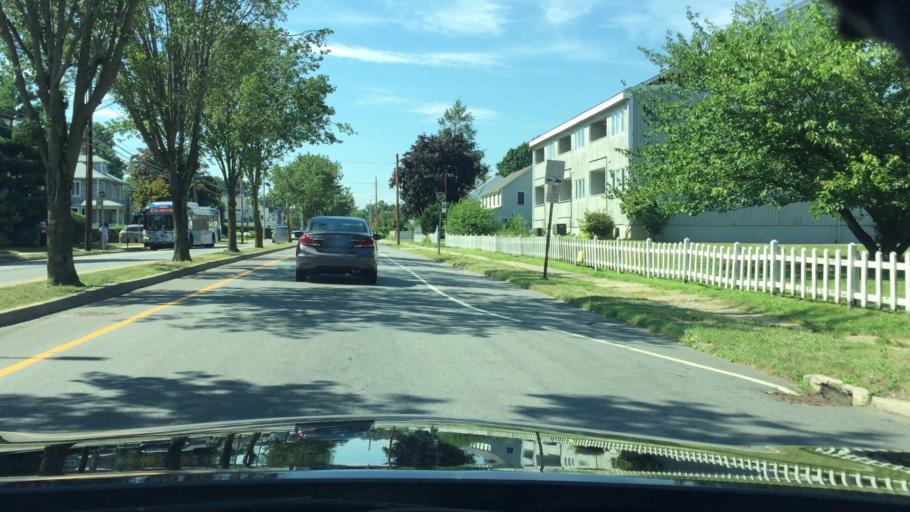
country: US
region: Connecticut
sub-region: Fairfield County
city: Trumbull
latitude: 41.2059
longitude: -73.2060
